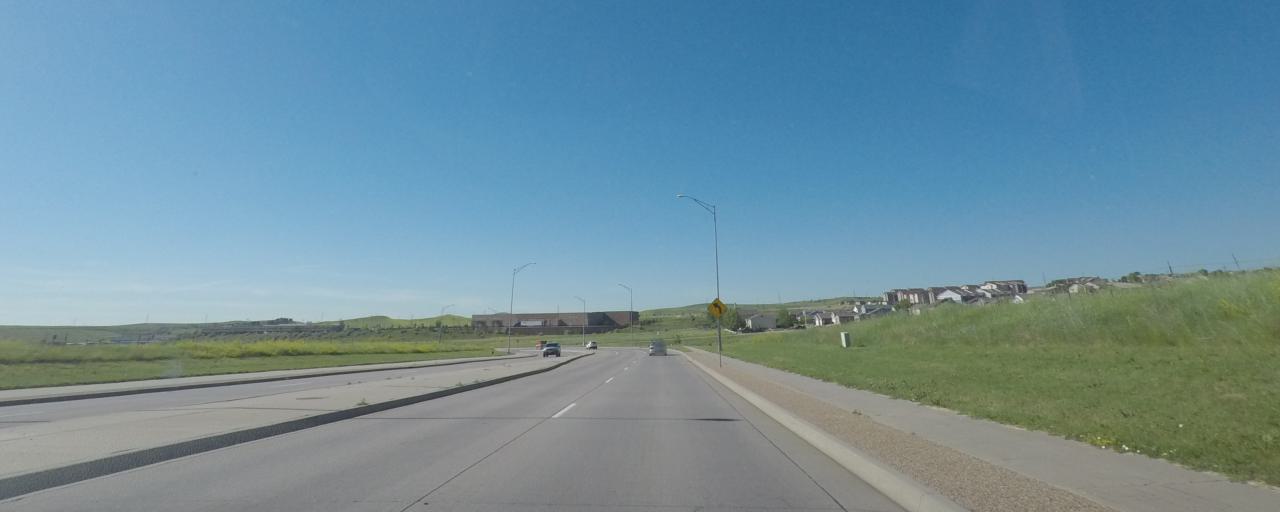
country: US
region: South Dakota
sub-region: Pennington County
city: Rapid City
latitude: 44.0391
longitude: -103.2191
